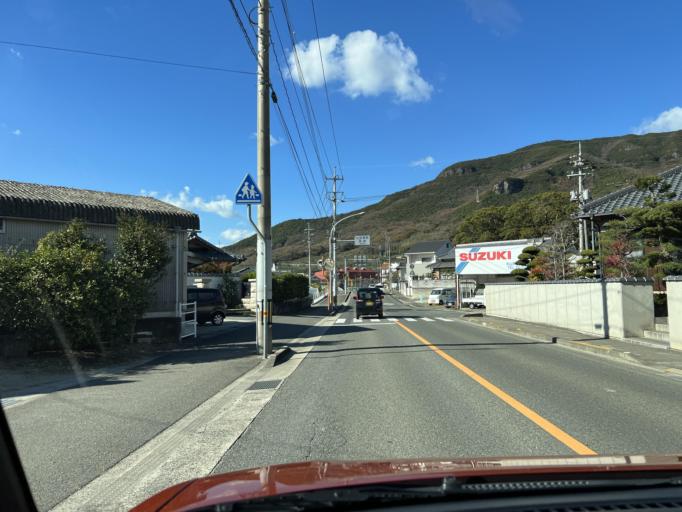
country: JP
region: Kagawa
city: Tonosho
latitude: 34.4829
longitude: 134.2375
